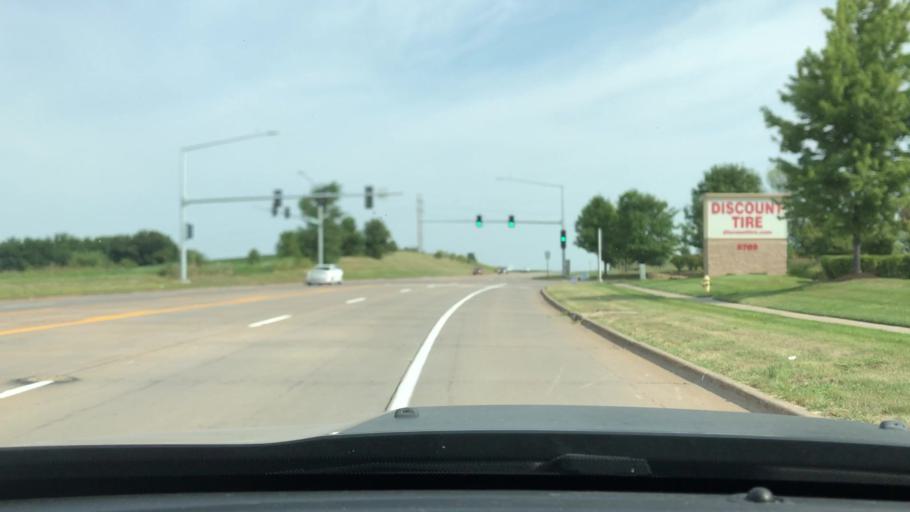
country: US
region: Iowa
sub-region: Scott County
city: Bettendorf
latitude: 41.5796
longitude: -90.5288
